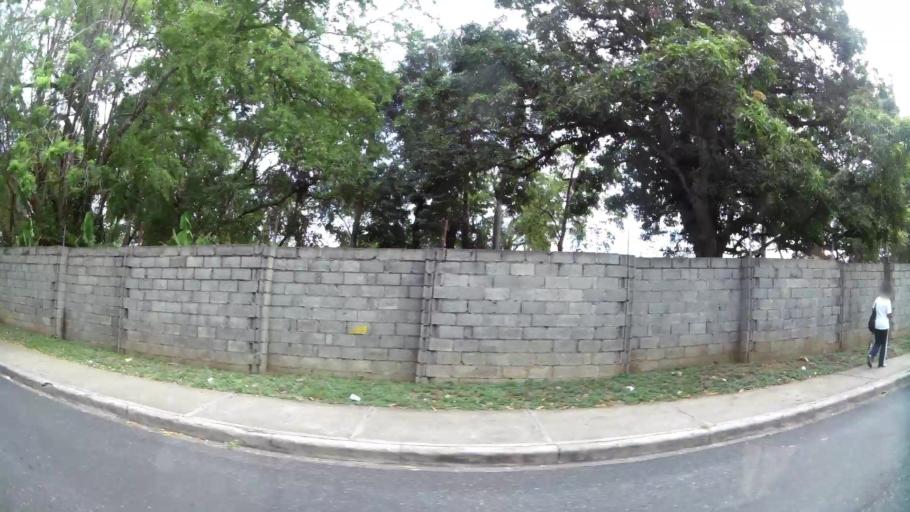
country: DO
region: Santiago
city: Santiago de los Caballeros
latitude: 19.4599
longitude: -70.6893
